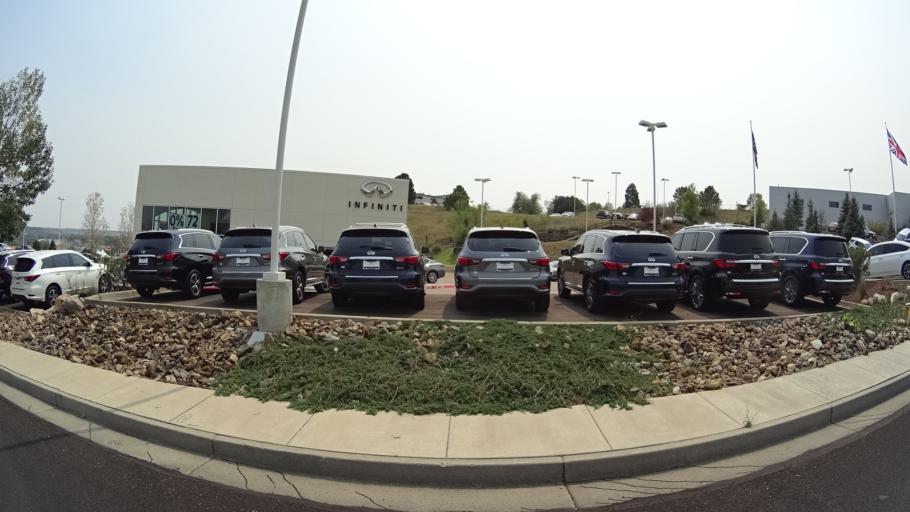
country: US
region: Colorado
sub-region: El Paso County
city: Colorado Springs
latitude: 38.8161
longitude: -104.8367
